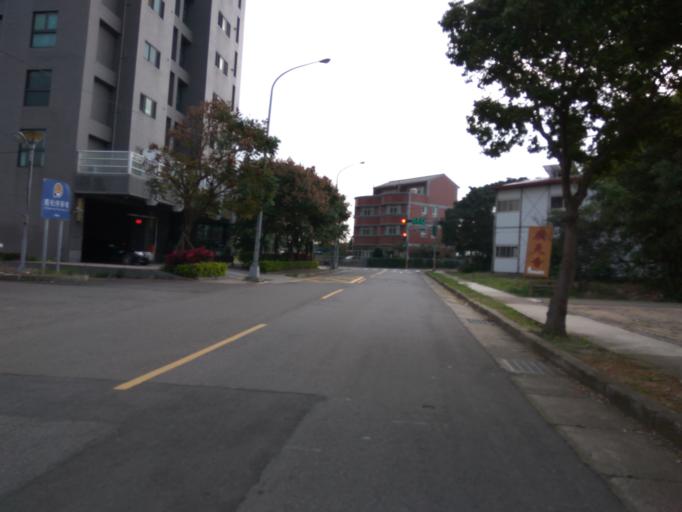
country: TW
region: Taiwan
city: Taoyuan City
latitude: 25.0051
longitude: 121.2155
